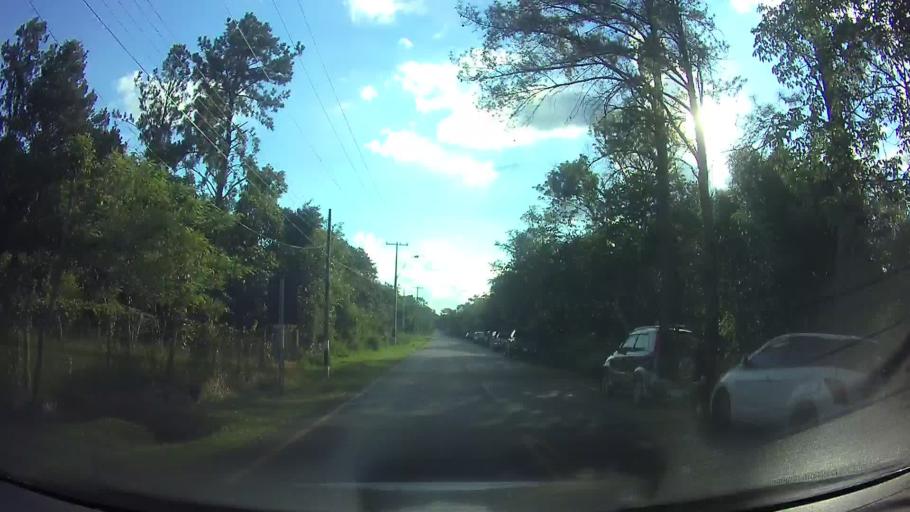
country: PY
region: Central
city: Aregua
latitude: -25.2694
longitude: -57.4272
